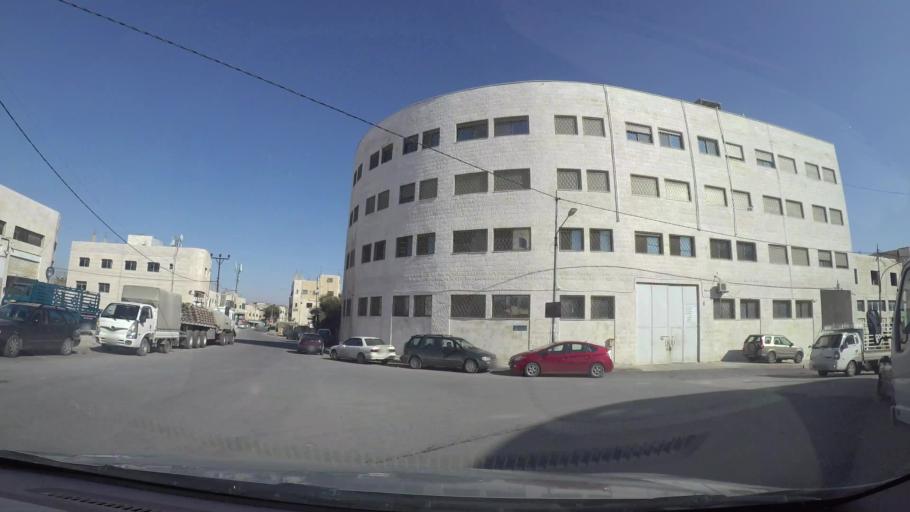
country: JO
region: Amman
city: Al Bunayyat ash Shamaliyah
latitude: 31.9086
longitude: 35.8999
